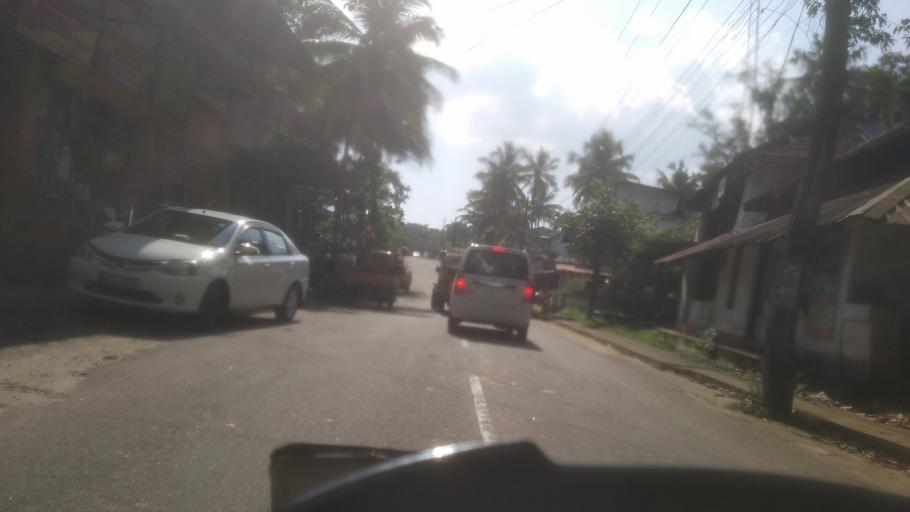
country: IN
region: Kerala
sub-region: Ernakulam
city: Kotamangalam
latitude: 10.0076
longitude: 76.7121
